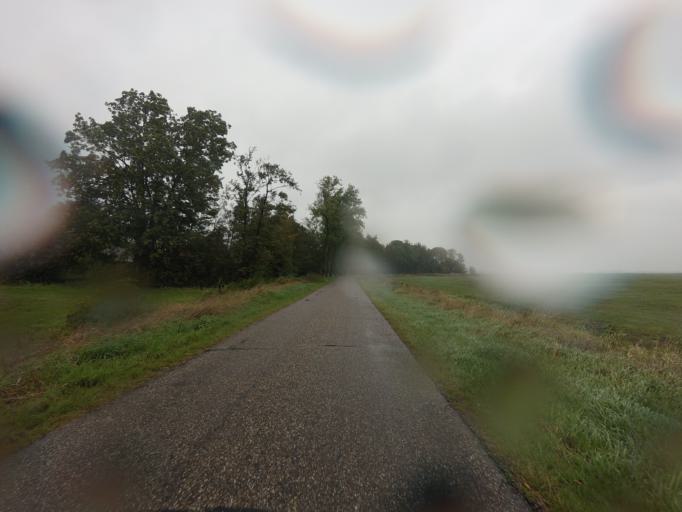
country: NL
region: Friesland
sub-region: Gemeente Boarnsterhim
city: Aldeboarn
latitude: 53.0735
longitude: 5.9285
